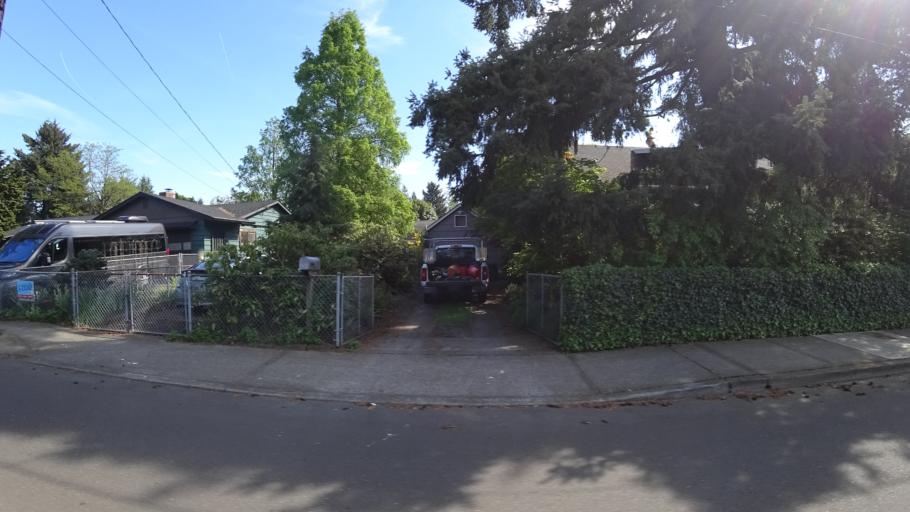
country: US
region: Oregon
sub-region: Clackamas County
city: Milwaukie
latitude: 45.4585
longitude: -122.6277
